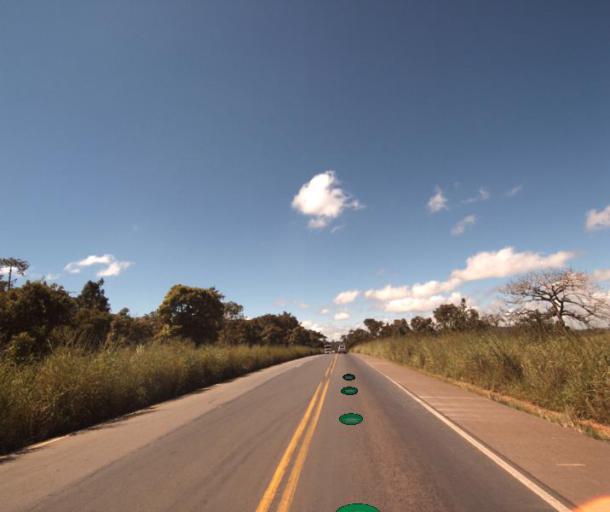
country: BR
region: Goias
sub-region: Jaragua
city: Jaragua
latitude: -15.6413
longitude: -49.3714
